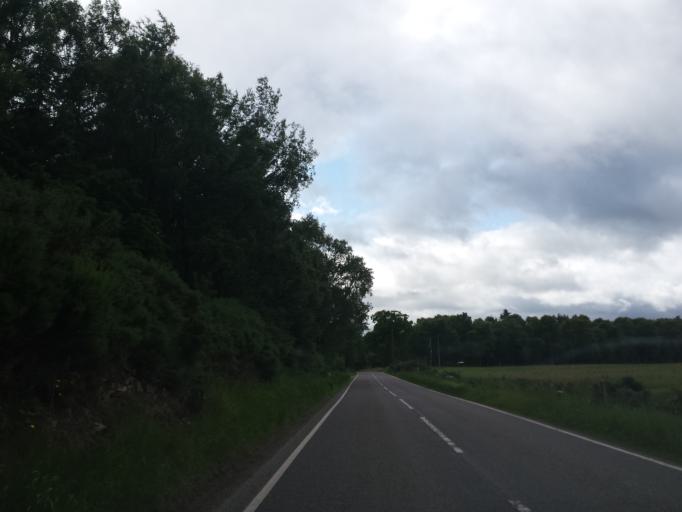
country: GB
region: Scotland
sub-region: Highland
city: Fortrose
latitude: 57.5107
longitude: -4.0200
